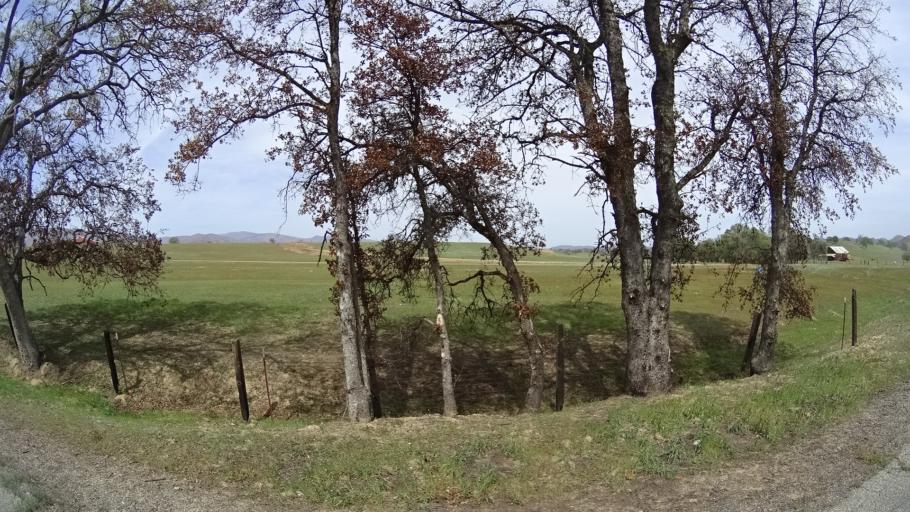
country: US
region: California
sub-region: Glenn County
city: Willows
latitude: 39.5916
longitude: -122.5638
